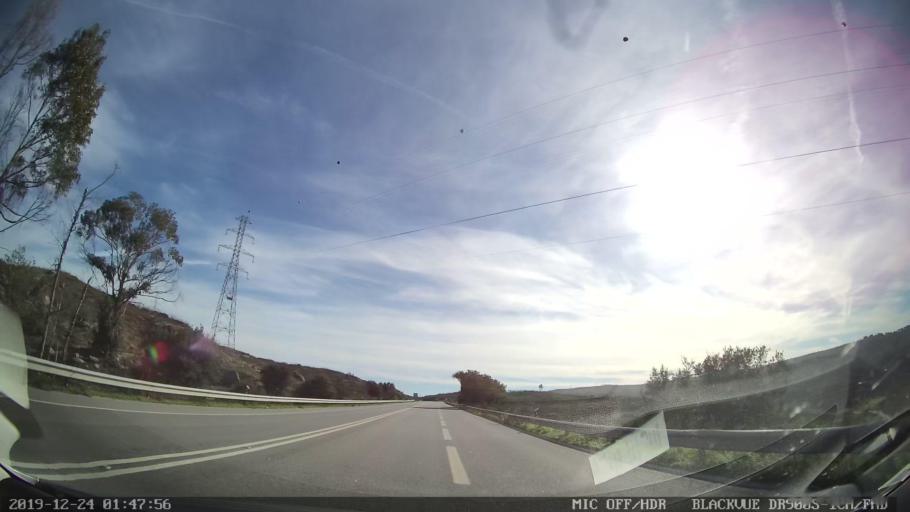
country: PT
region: Portalegre
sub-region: Nisa
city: Nisa
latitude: 39.5262
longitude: -7.7851
